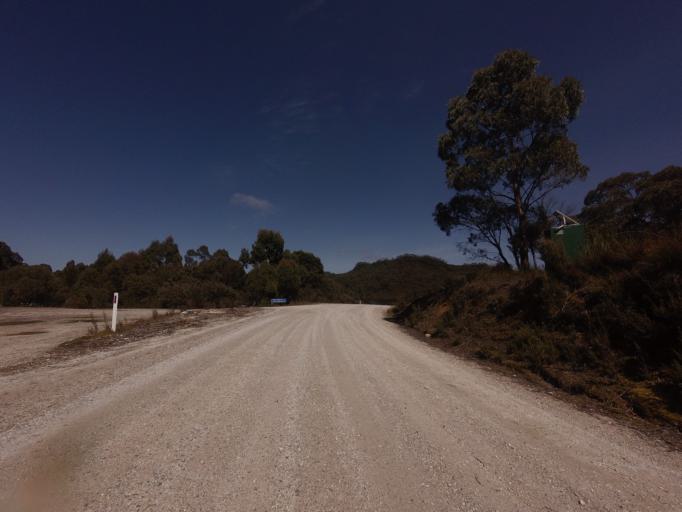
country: AU
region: Tasmania
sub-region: Huon Valley
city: Geeveston
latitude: -43.0292
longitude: 146.3503
